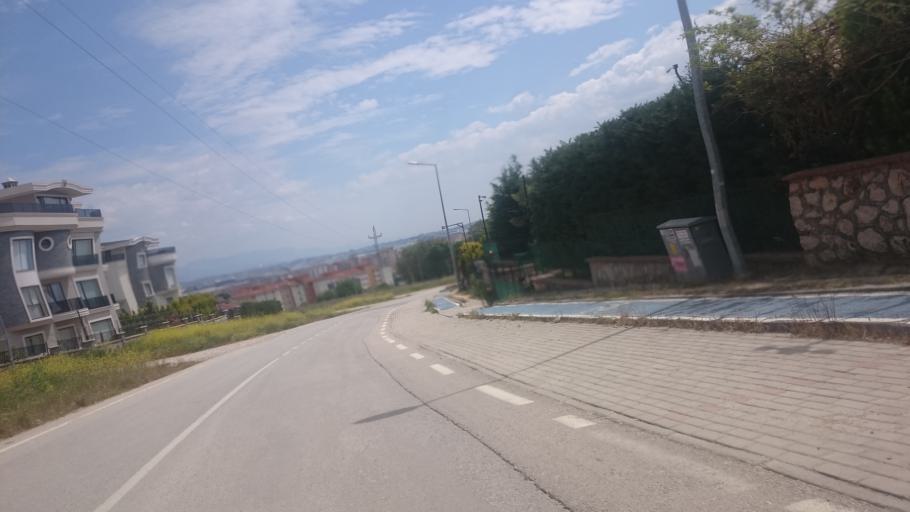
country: TR
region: Bursa
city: Gorukle
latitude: 40.2283
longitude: 28.8949
